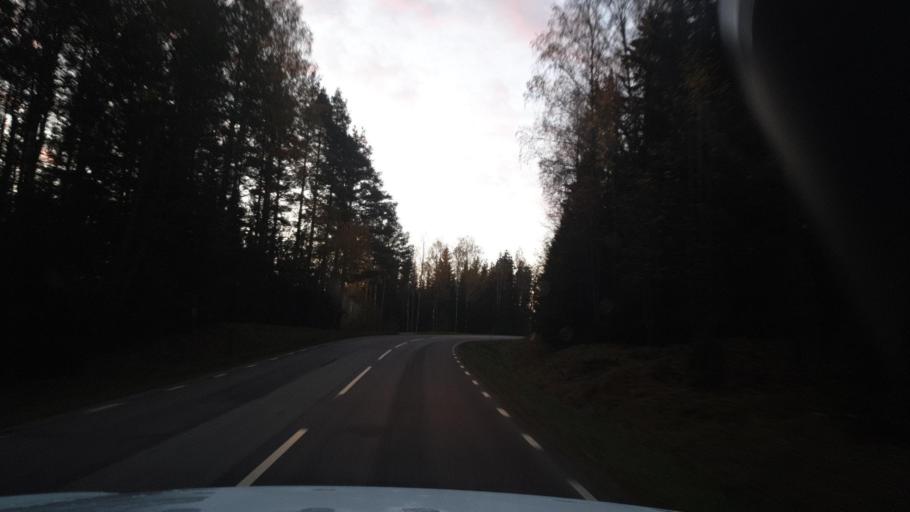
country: SE
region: Vaermland
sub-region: Eda Kommun
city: Charlottenberg
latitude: 59.7897
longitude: 12.2581
